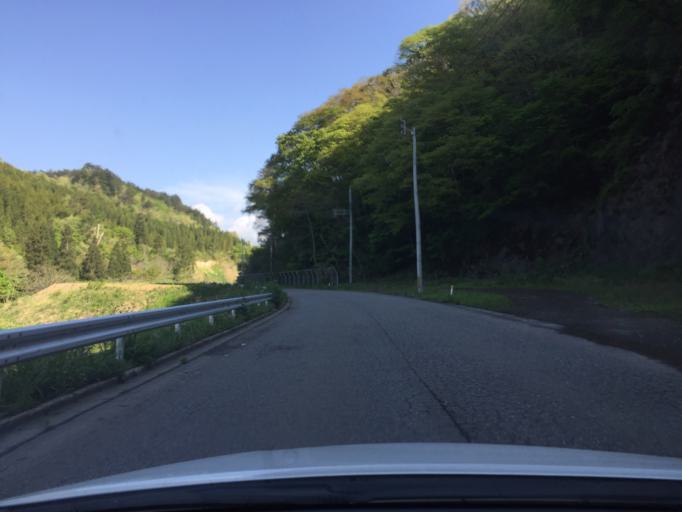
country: JP
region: Fukushima
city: Kitakata
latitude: 37.6723
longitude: 139.7297
